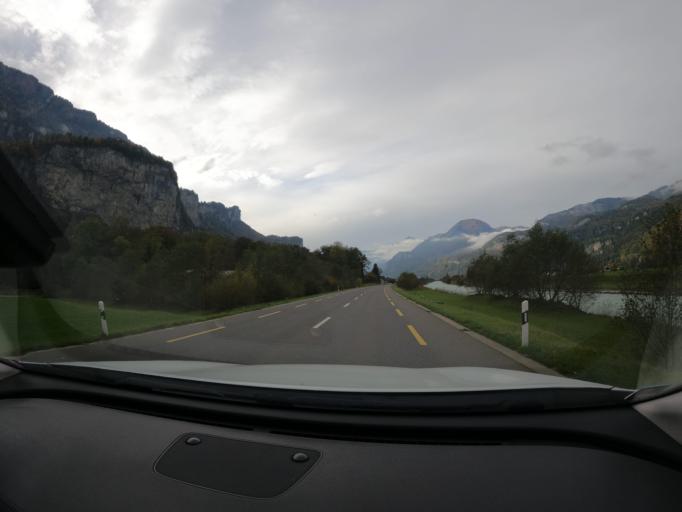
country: CH
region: Bern
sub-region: Interlaken-Oberhasli District
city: Meiringen
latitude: 46.7242
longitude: 8.1763
